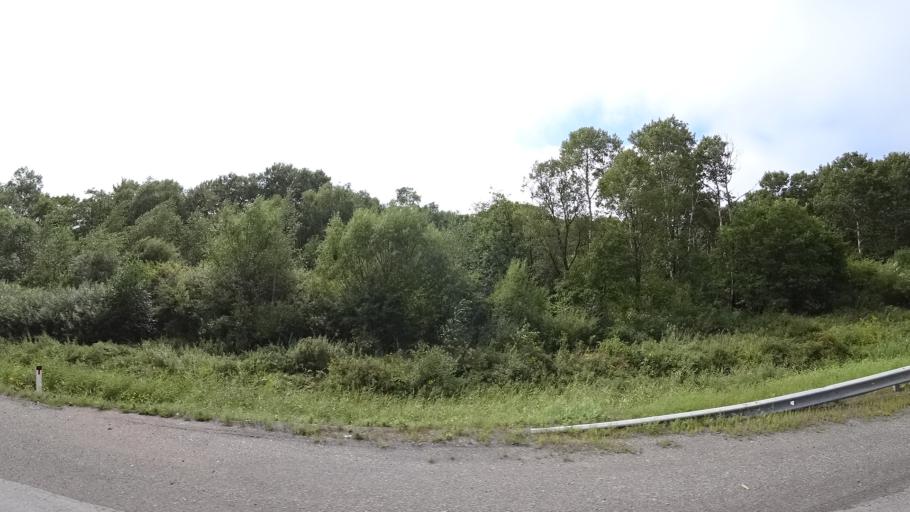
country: RU
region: Primorskiy
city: Lyalichi
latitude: 44.1095
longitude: 132.4200
